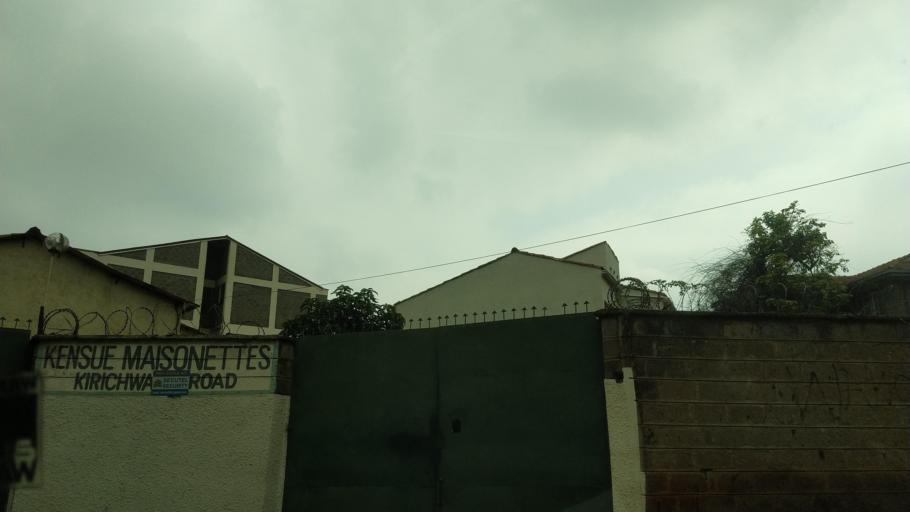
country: KE
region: Nairobi Area
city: Nairobi
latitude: -1.2931
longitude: 36.7817
